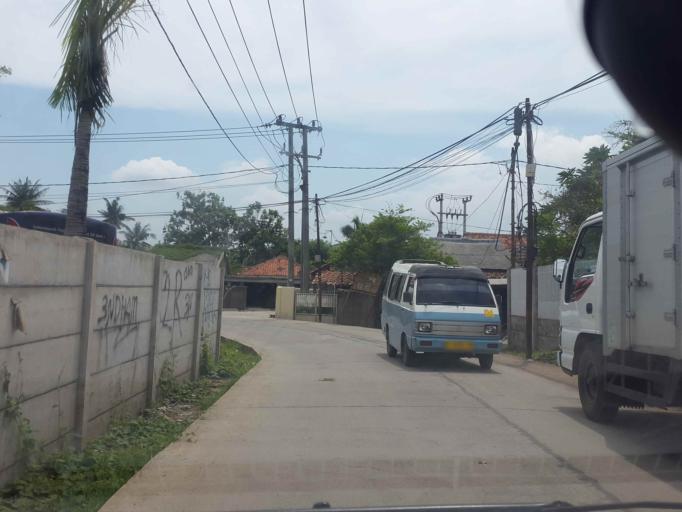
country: ID
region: West Java
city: Teluknaga
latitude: -6.1278
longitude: 106.6158
